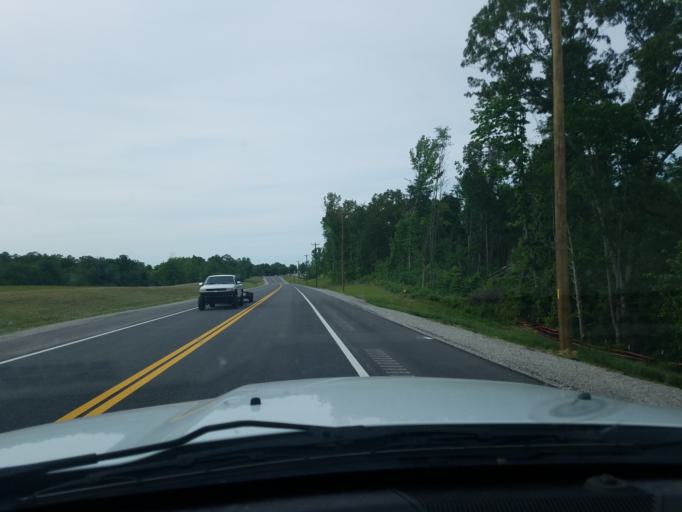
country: US
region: Tennessee
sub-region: Putnam County
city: Cookeville
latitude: 36.1707
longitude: -85.5619
